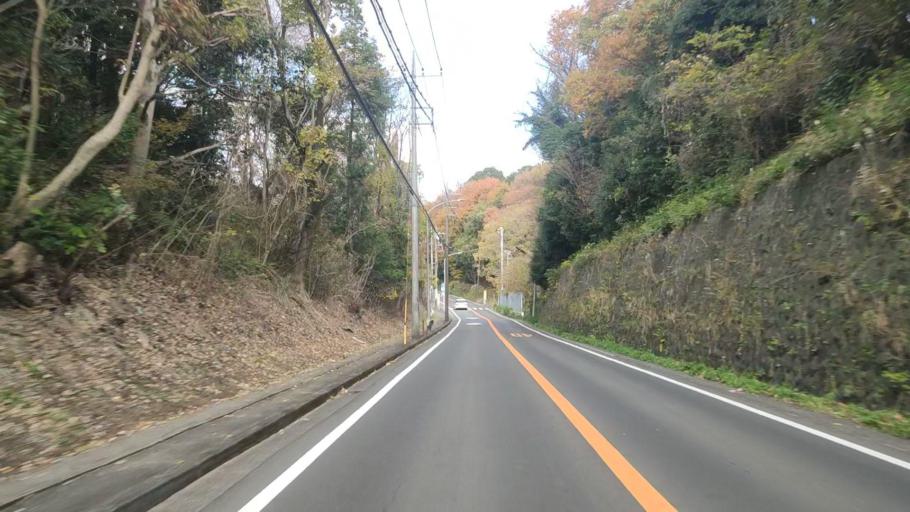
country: JP
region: Kanagawa
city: Minami-rinkan
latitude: 35.4831
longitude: 139.5039
